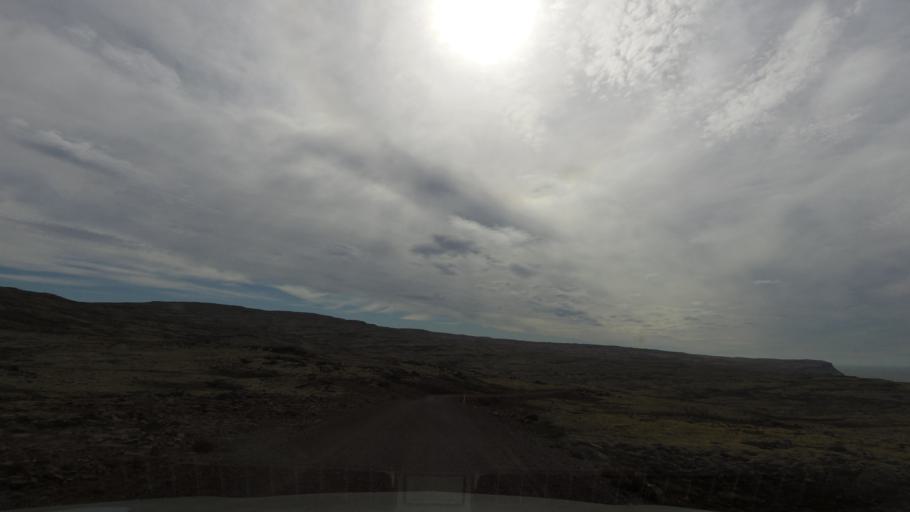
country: IS
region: West
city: Olafsvik
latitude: 65.5452
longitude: -24.2814
